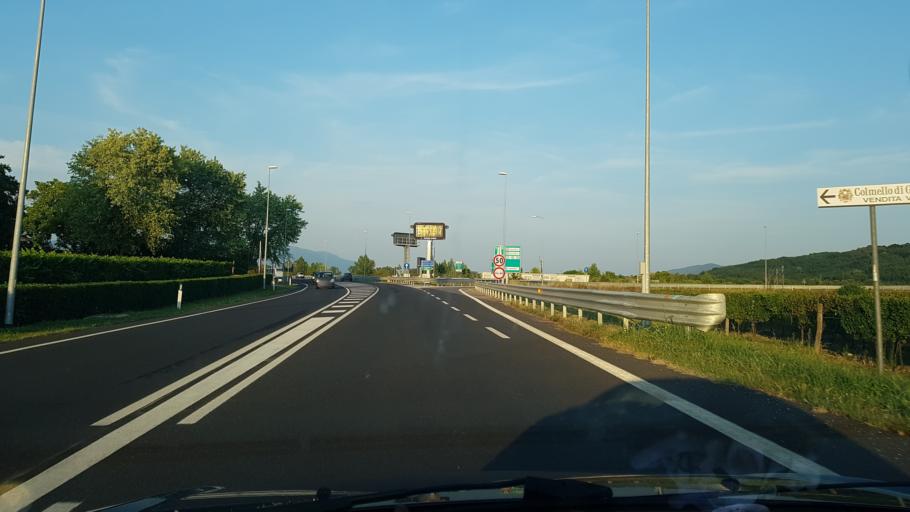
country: IT
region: Friuli Venezia Giulia
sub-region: Provincia di Gorizia
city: Farra d'Isonzo
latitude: 45.9044
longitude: 13.5442
